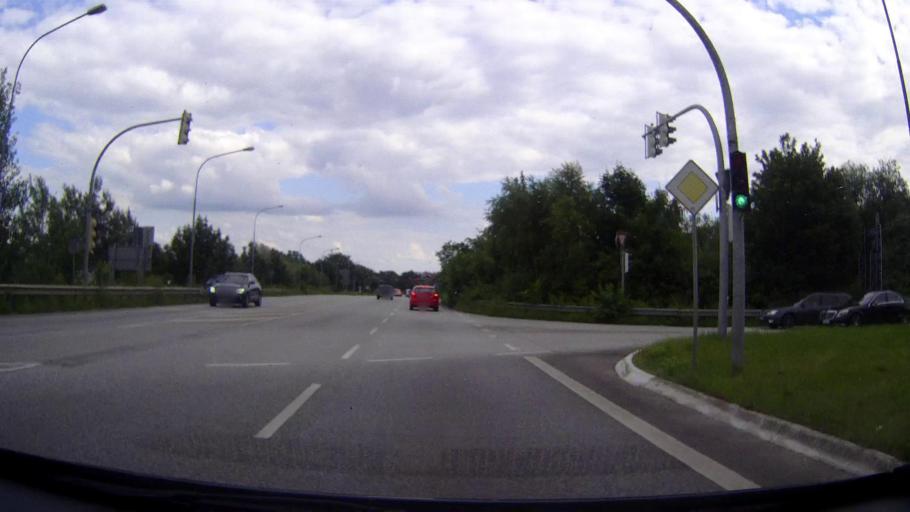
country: DE
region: Schleswig-Holstein
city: Stockelsdorf
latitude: 53.8623
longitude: 10.6245
